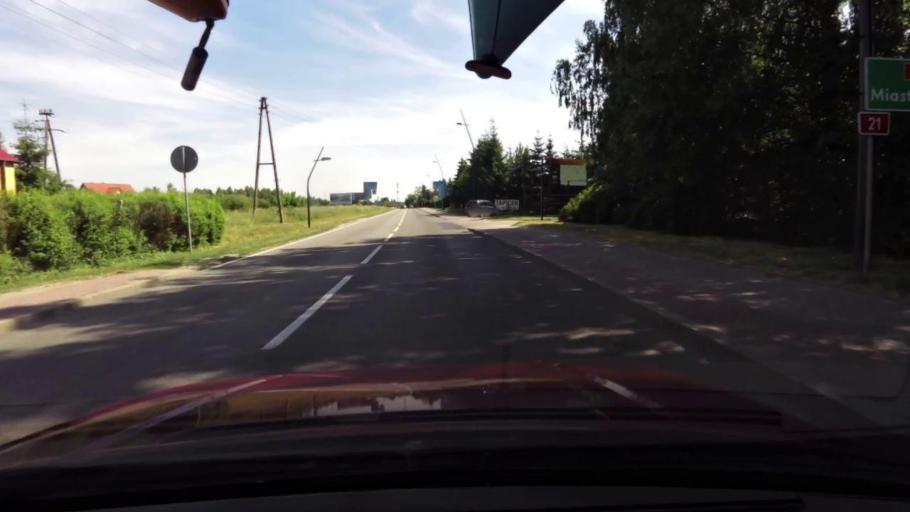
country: PL
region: Pomeranian Voivodeship
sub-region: Powiat slupski
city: Kobylnica
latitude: 54.4374
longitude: 16.9974
